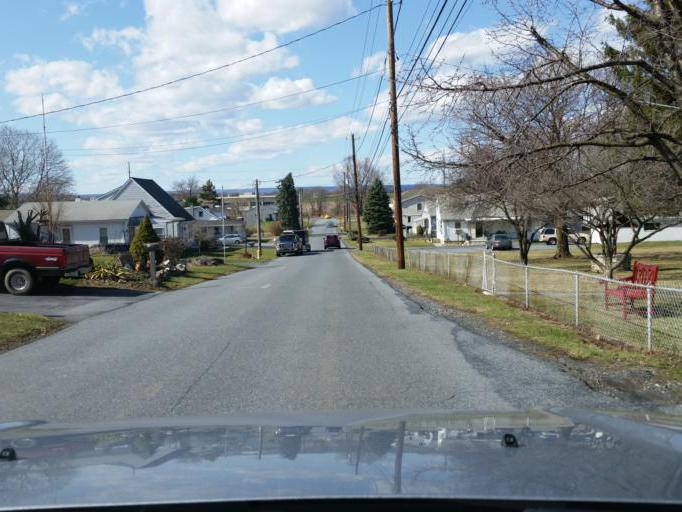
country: US
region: Pennsylvania
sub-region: Dauphin County
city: Hummelstown
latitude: 40.2701
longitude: -76.6832
